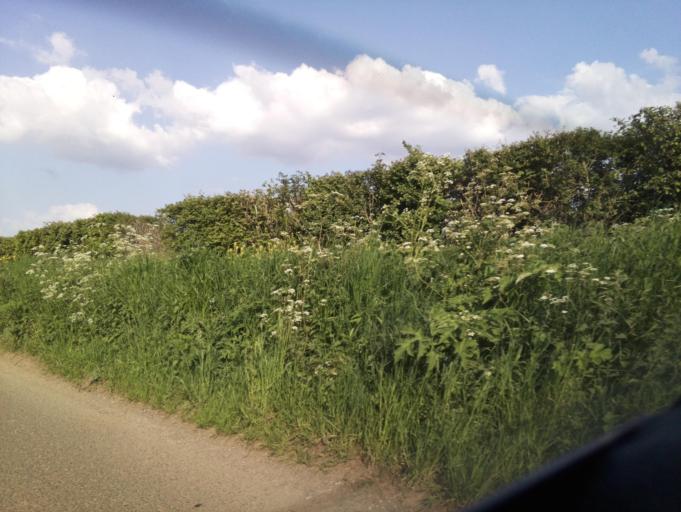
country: GB
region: England
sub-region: Wiltshire
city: Biddestone
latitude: 51.4842
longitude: -2.1653
